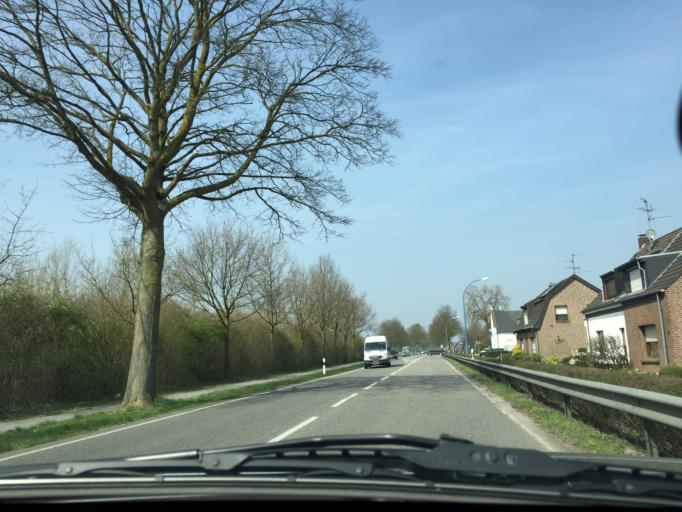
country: DE
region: North Rhine-Westphalia
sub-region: Regierungsbezirk Dusseldorf
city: Kleve
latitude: 51.7581
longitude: 6.1515
